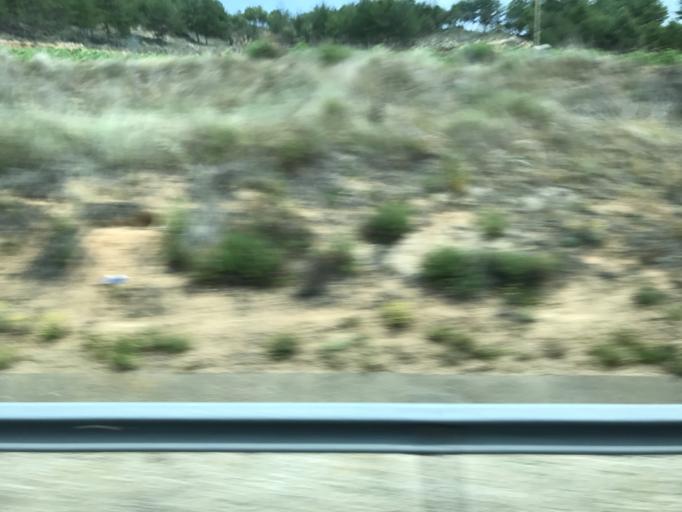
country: ES
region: Castille and Leon
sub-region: Provincia de Burgos
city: Oquillas
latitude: 41.7881
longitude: -3.6982
